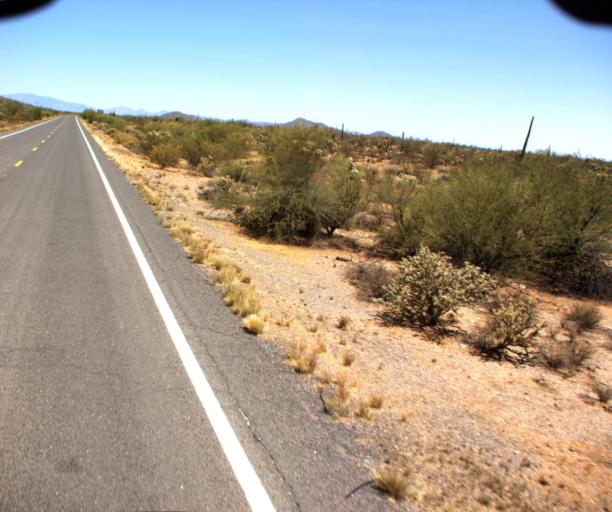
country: US
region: Arizona
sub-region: Pinal County
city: Florence
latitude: 32.7964
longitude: -111.1790
